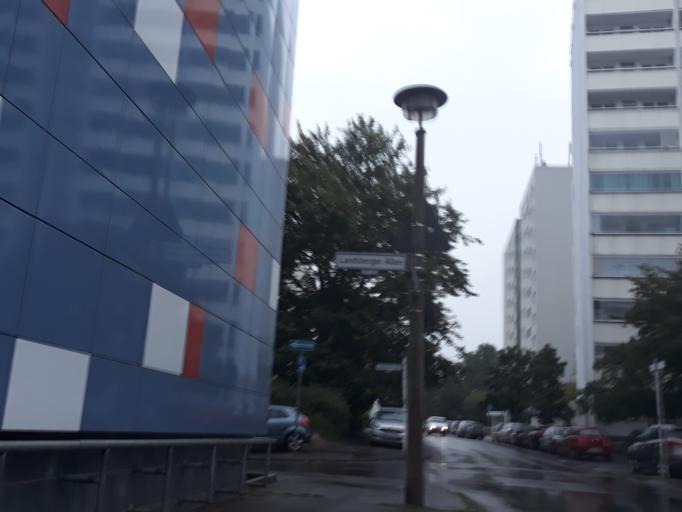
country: DE
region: Berlin
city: Fennpfuhl
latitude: 52.5316
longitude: 13.4825
